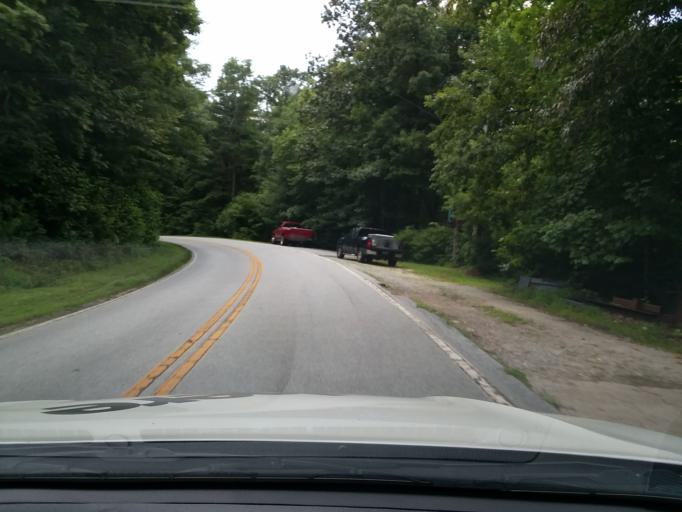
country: US
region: Georgia
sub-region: Rabun County
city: Mountain City
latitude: 35.0034
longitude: -83.2018
